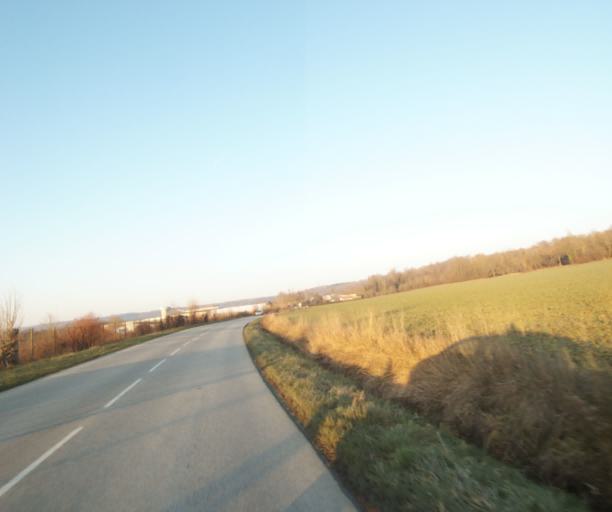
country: FR
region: Champagne-Ardenne
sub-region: Departement de la Haute-Marne
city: Bienville
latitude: 48.5945
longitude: 5.0417
